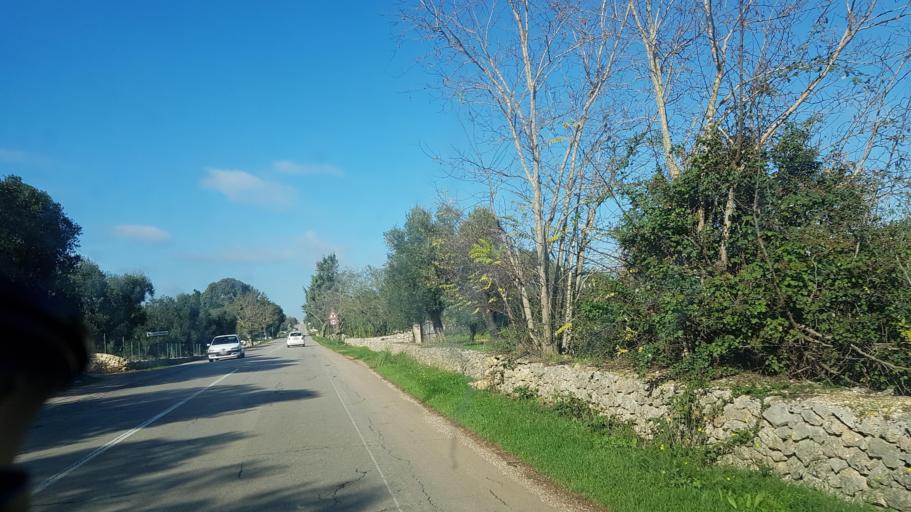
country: IT
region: Apulia
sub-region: Provincia di Brindisi
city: Carovigno
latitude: 40.6822
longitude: 17.6821
